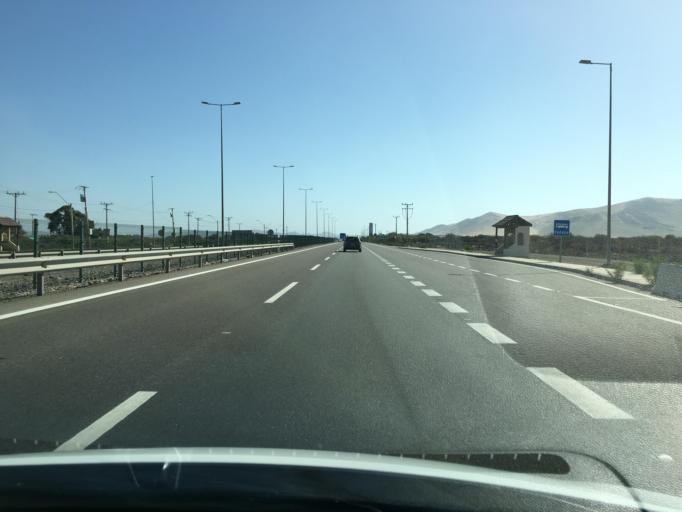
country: CL
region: Atacama
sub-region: Provincia de Copiapo
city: Copiapo
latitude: -27.3384
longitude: -70.5997
